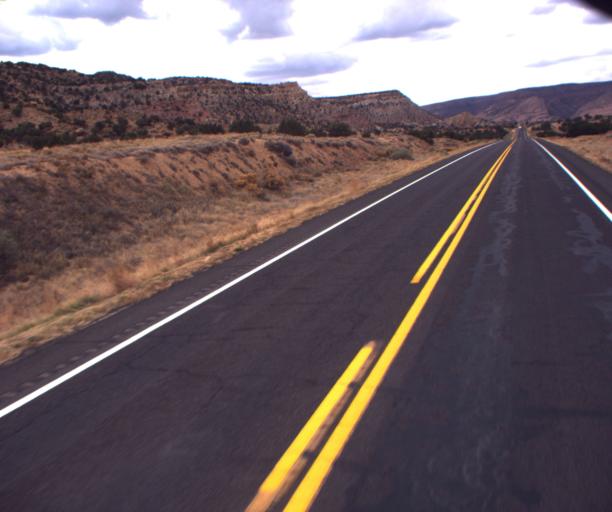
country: US
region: Arizona
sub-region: Navajo County
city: Kayenta
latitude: 36.6974
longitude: -110.3419
